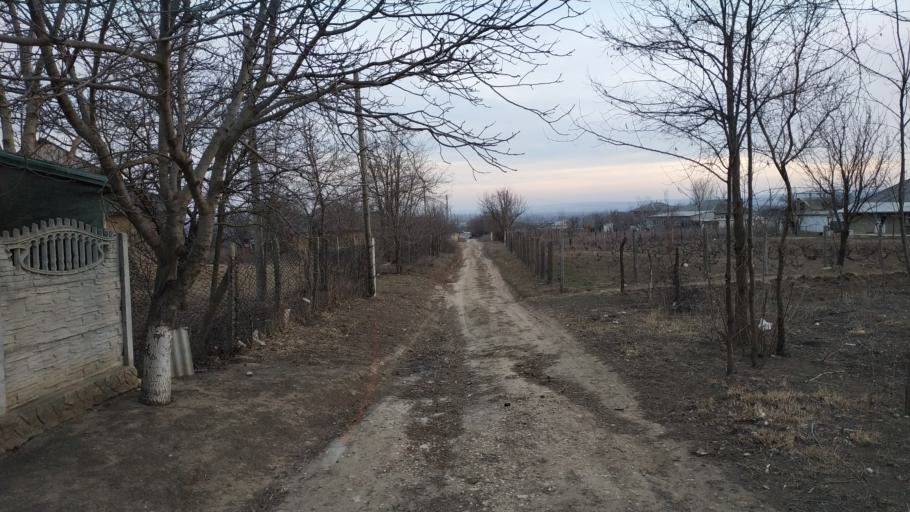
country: MD
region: Hincesti
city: Dancu
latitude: 46.7497
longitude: 28.2107
